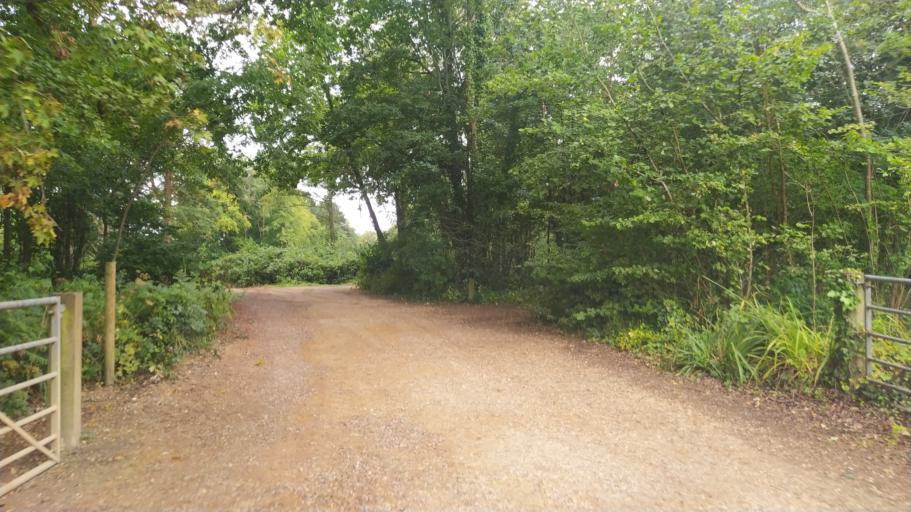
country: GB
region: England
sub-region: Hampshire
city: Hedge End
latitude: 50.8988
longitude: -1.2924
